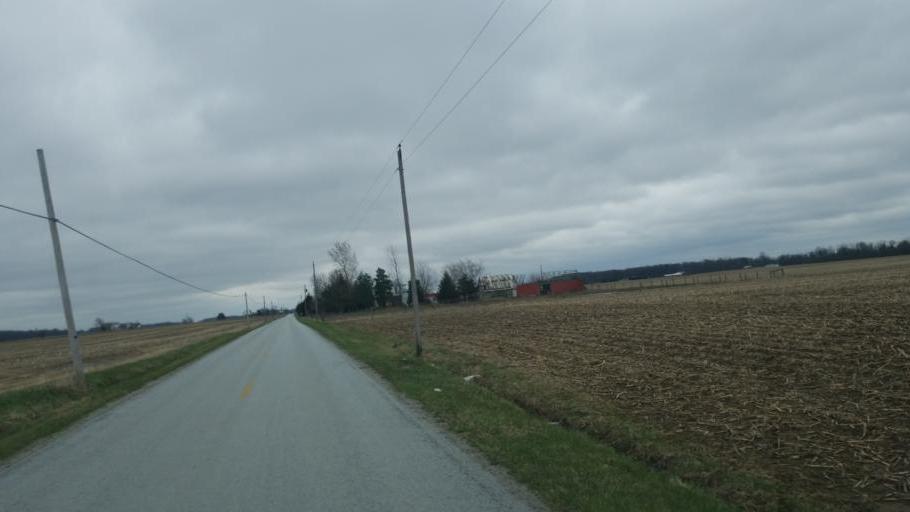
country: US
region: Ohio
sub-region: Hardin County
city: Kenton
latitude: 40.6577
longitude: -83.5089
